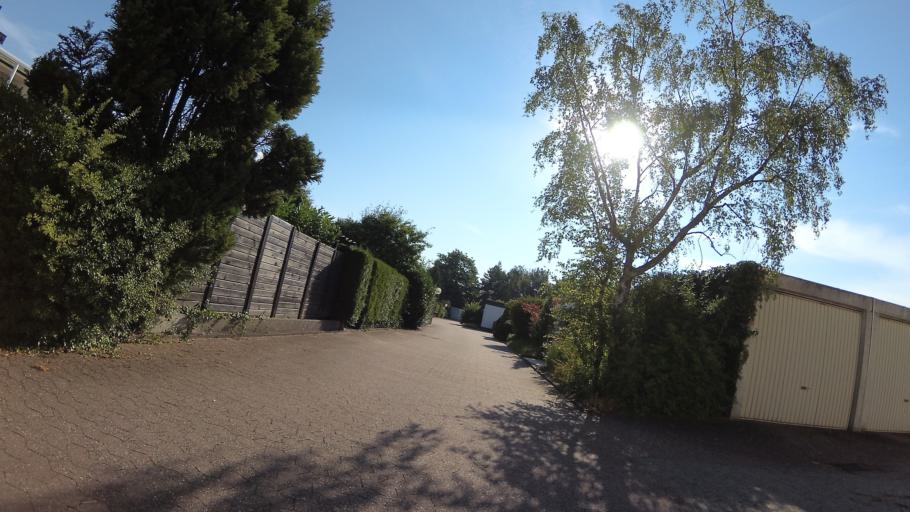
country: DE
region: Saarland
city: Homburg
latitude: 49.3367
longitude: 7.3202
